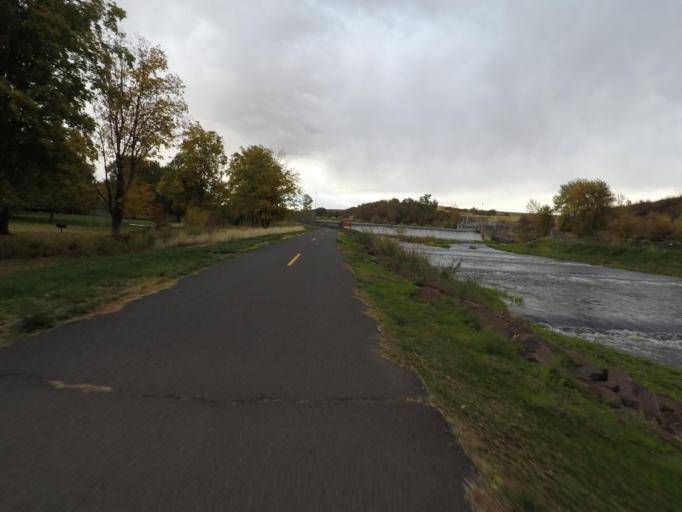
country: US
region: Washington
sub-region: Walla Walla County
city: Walla Walla East
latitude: 46.0802
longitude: -118.2564
